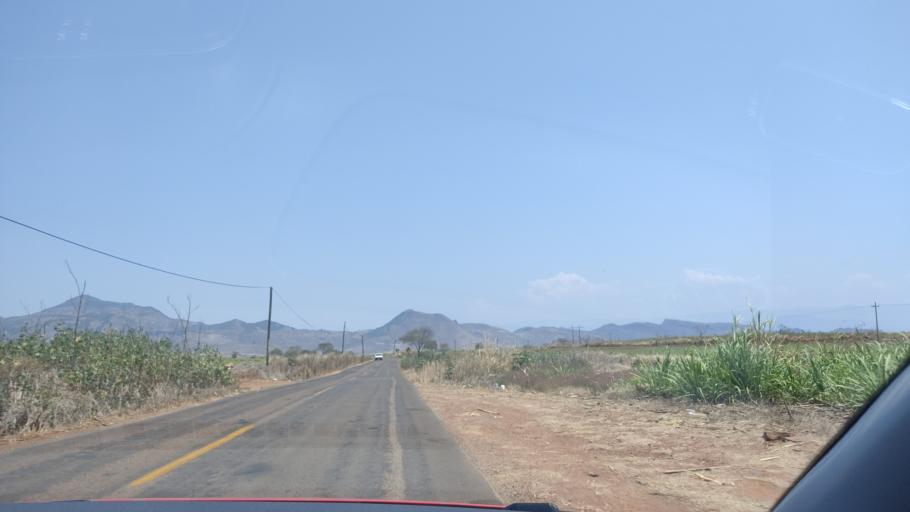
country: MX
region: Nayarit
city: Puga
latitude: 21.5860
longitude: -104.7509
